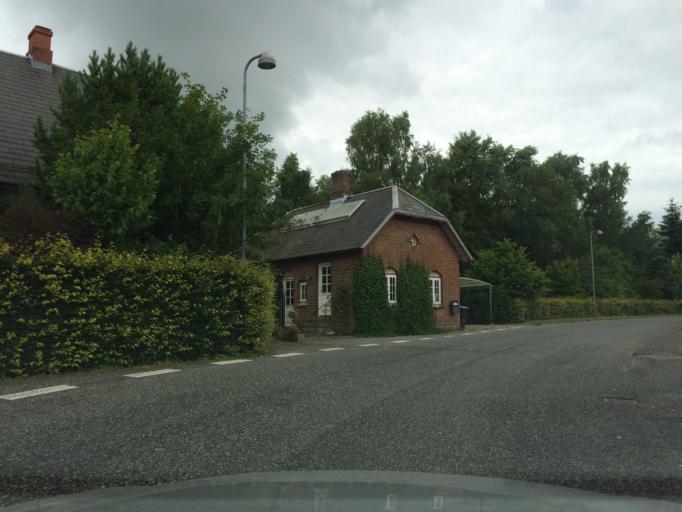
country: DK
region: Central Jutland
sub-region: Favrskov Kommune
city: Hammel
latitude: 56.2288
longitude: 9.7350
